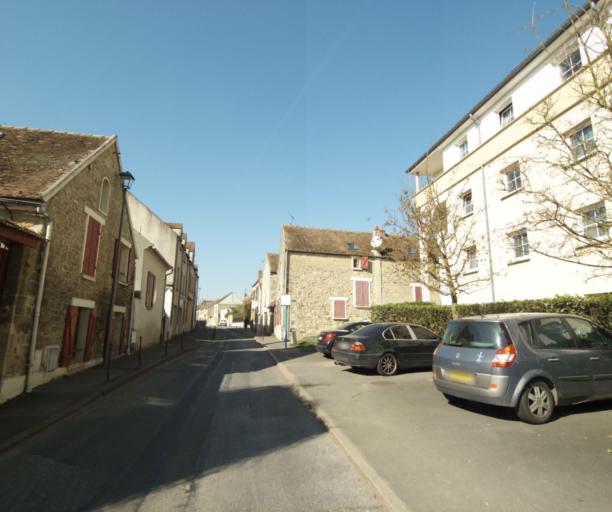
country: FR
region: Ile-de-France
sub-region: Departement du Val-d'Oise
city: Cergy
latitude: 49.0328
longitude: 2.0636
